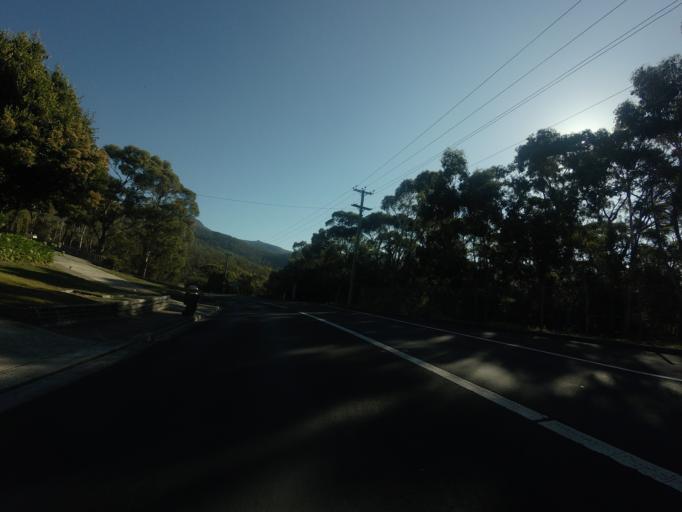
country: AU
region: Tasmania
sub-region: Glenorchy
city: West Moonah
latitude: -42.8623
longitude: 147.2754
